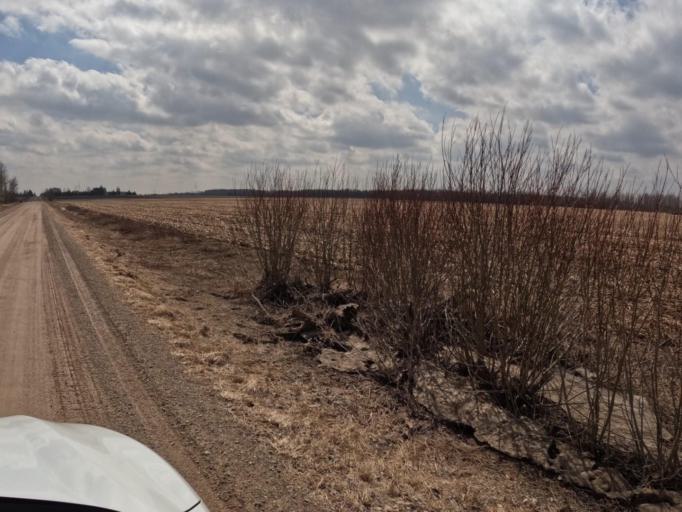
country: CA
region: Ontario
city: Shelburne
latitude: 44.0266
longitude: -80.3311
